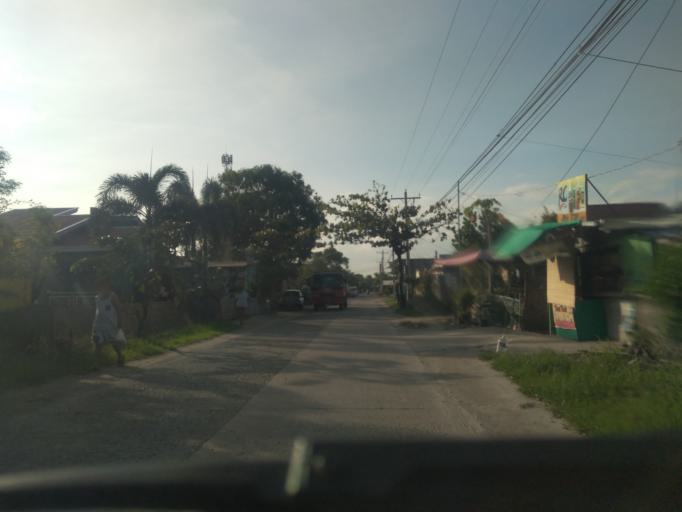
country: PH
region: Central Luzon
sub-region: Province of Pampanga
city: Bulaon
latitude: 15.0888
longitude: 120.6907
